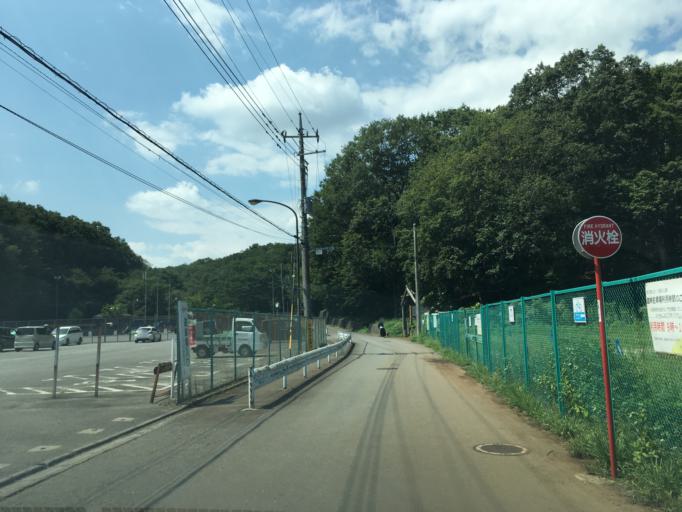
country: JP
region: Tokyo
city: Fussa
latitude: 35.7635
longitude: 139.3863
